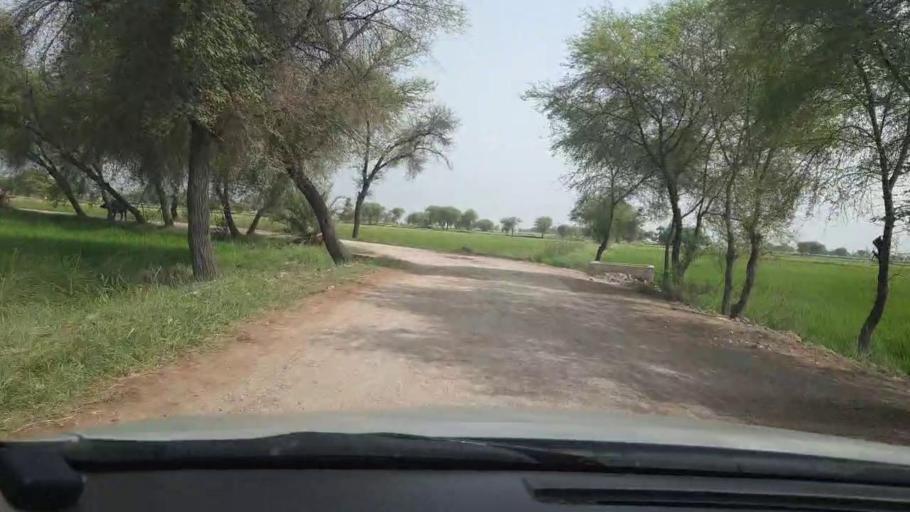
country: PK
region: Sindh
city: Shikarpur
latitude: 28.0000
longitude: 68.5952
